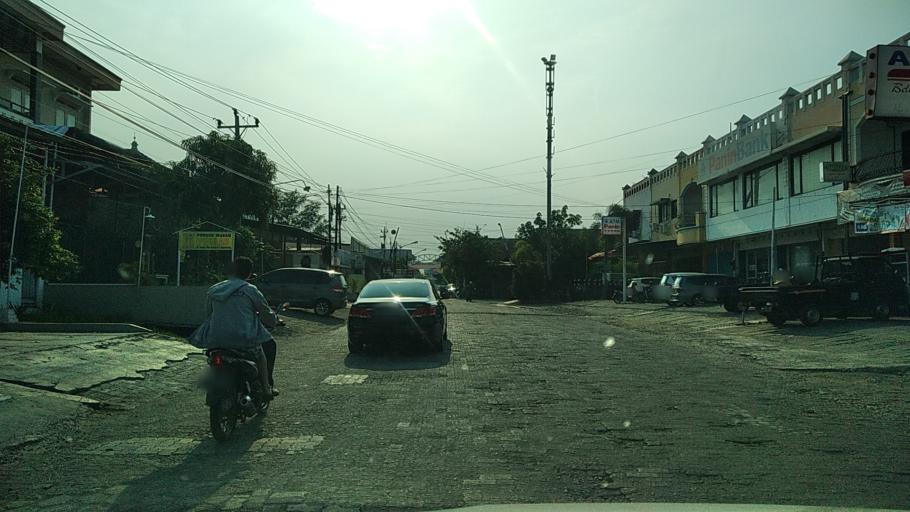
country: ID
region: Central Java
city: Semarang
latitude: -6.9591
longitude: 110.4083
